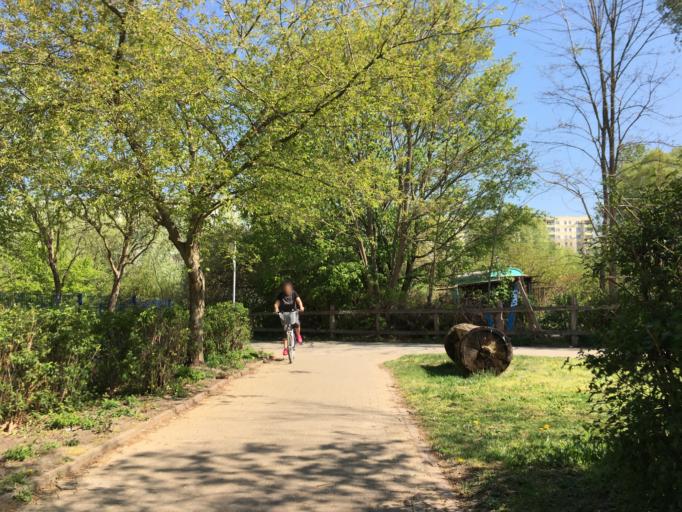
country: DE
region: Berlin
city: Buch
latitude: 52.6294
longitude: 13.4922
